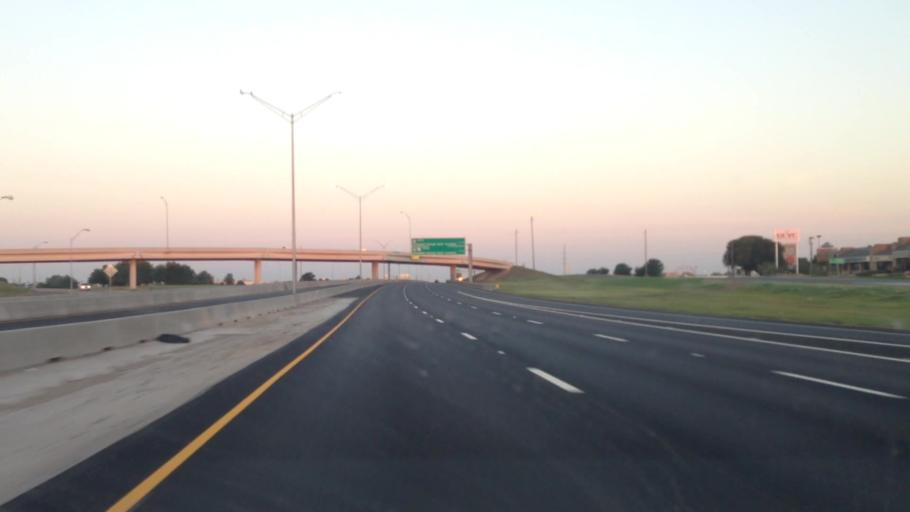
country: US
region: Texas
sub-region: Dallas County
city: Irving
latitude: 32.8374
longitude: -96.9869
